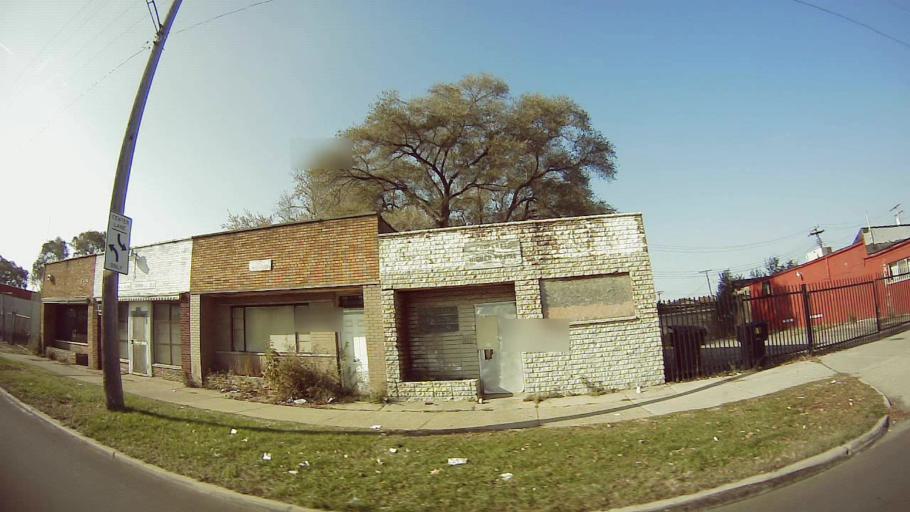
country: US
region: Michigan
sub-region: Oakland County
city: Oak Park
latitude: 42.4087
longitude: -83.1795
